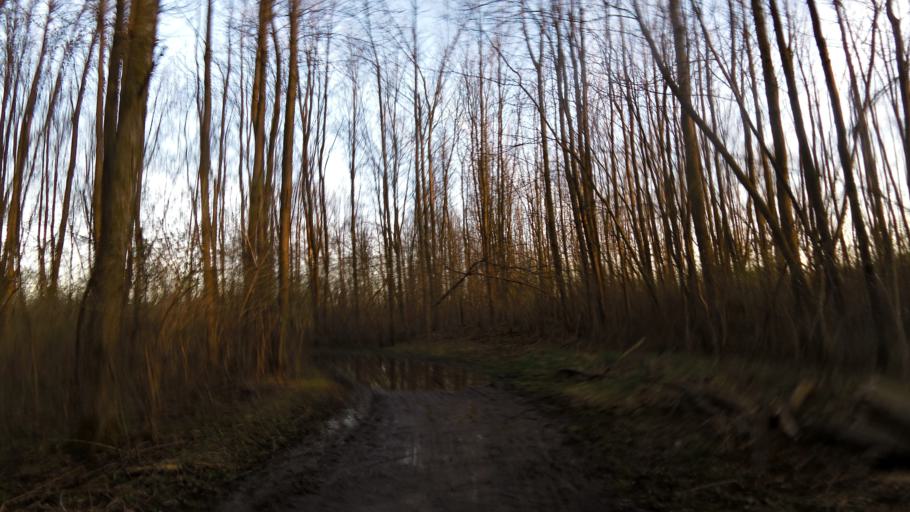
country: CA
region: Ontario
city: Bells Corners
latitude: 45.3428
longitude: -75.8901
